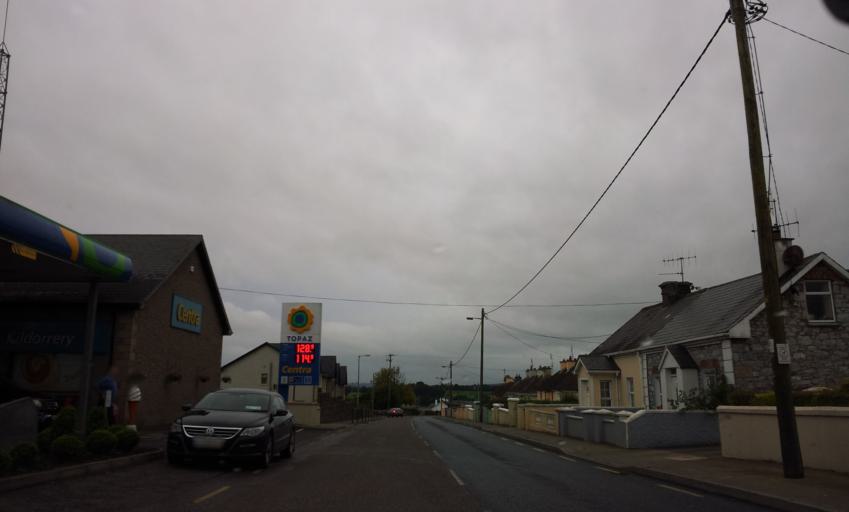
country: IE
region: Munster
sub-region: County Cork
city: Mitchelstown
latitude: 52.2459
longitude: -8.4289
